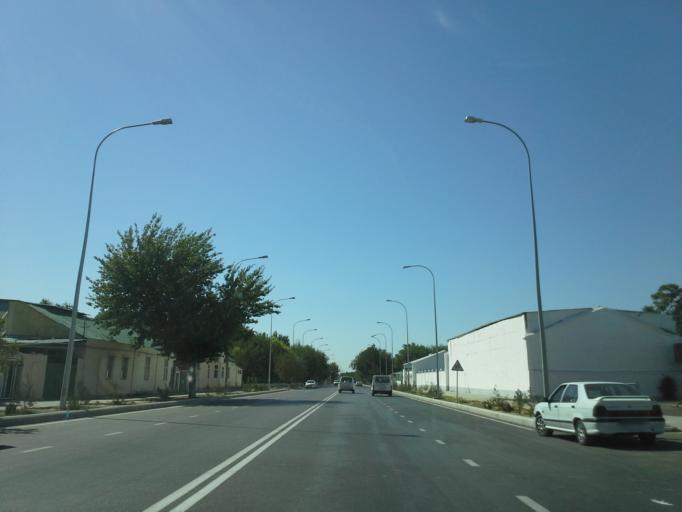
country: TM
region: Ahal
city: Ashgabat
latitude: 37.9543
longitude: 58.3840
